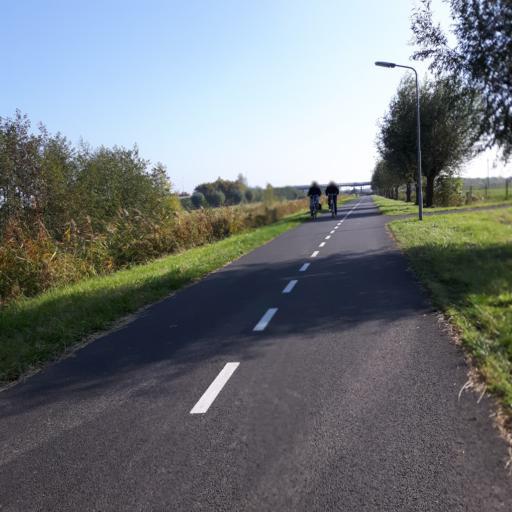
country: NL
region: Zeeland
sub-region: Gemeente Goes
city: Goes
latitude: 51.4933
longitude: 3.9216
